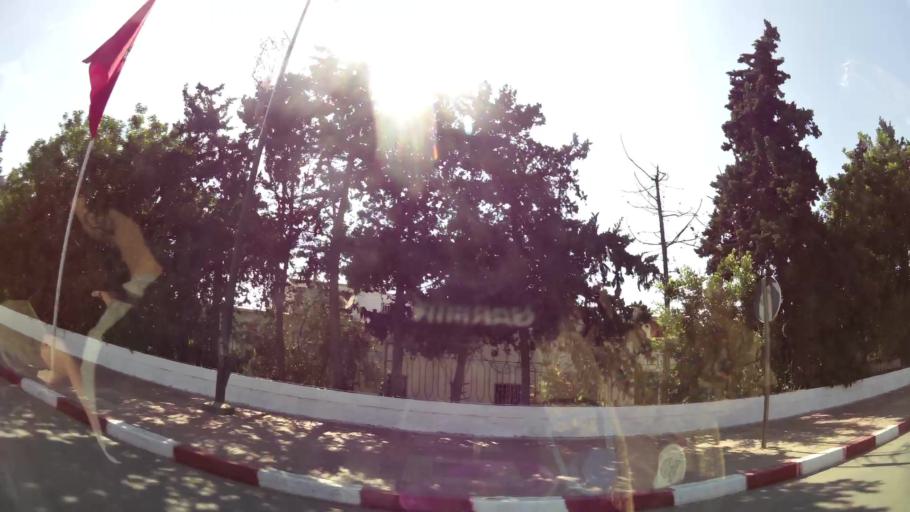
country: MA
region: Rabat-Sale-Zemmour-Zaer
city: Sale
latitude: 34.0438
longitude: -6.7746
